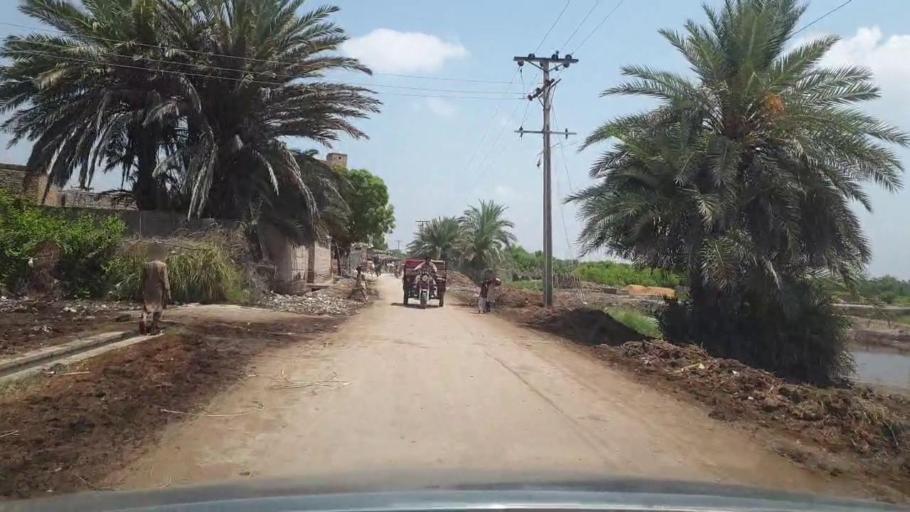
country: PK
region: Sindh
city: Pir jo Goth
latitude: 27.5990
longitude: 68.6052
